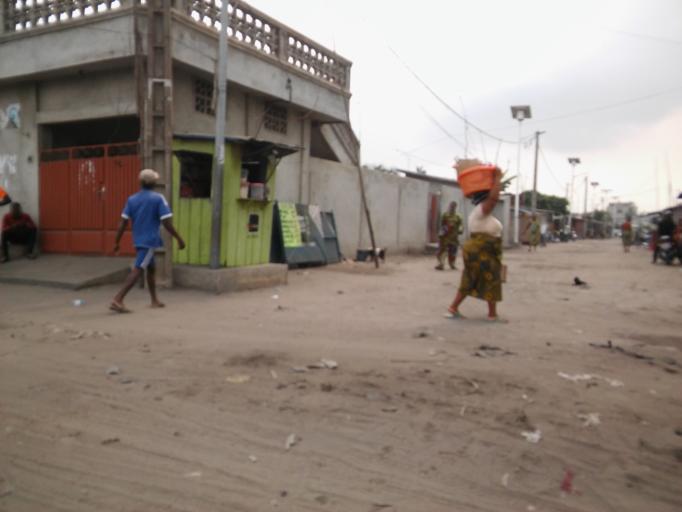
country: BJ
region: Littoral
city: Cotonou
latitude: 6.3870
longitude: 2.4238
